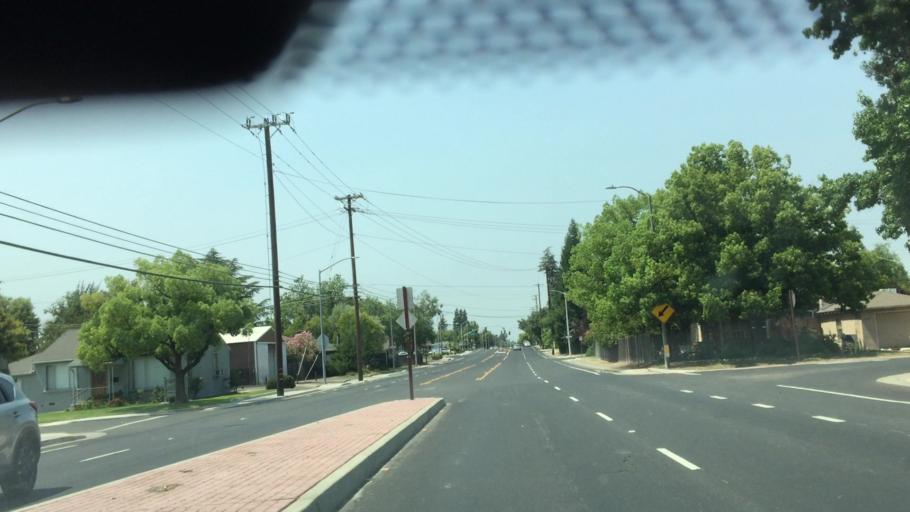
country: US
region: California
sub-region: Sacramento County
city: Arden-Arcade
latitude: 38.6103
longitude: -121.3655
